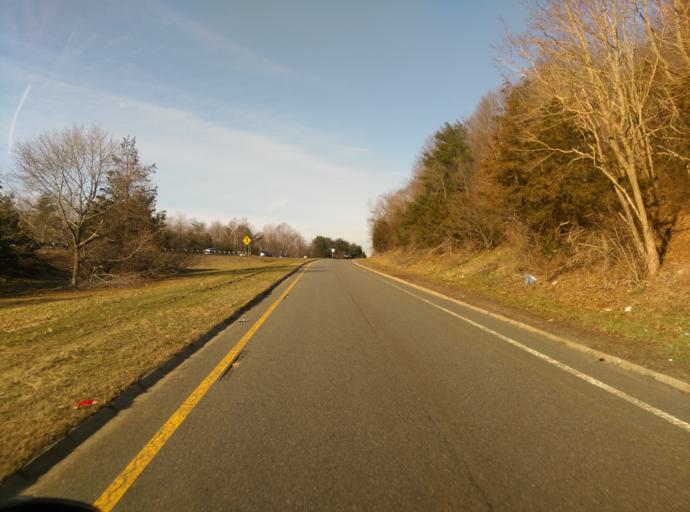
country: US
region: Massachusetts
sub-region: Essex County
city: Amesbury
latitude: 42.8401
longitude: -70.9383
